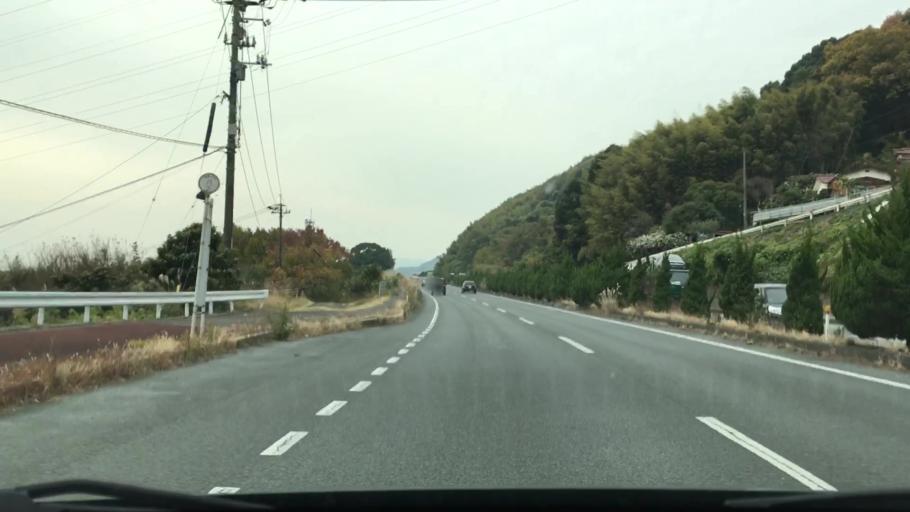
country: JP
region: Yamaguchi
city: Tokuyama
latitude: 34.0712
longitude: 131.7901
